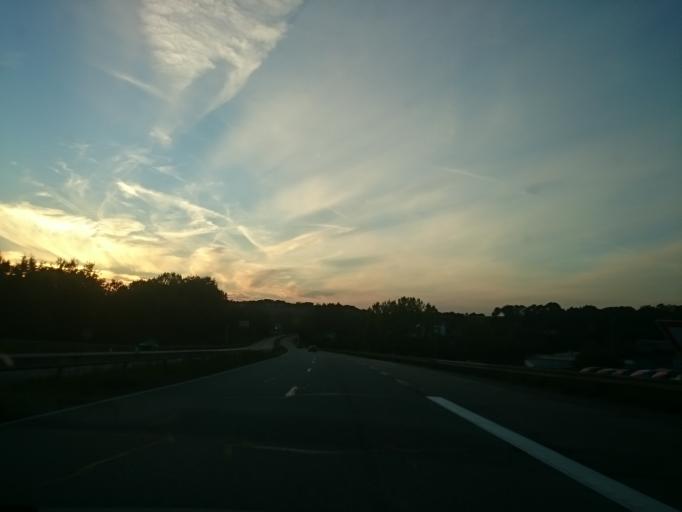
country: FR
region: Brittany
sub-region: Departement du Finistere
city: Ergue-Gaberic
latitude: 48.0019
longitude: -4.0532
